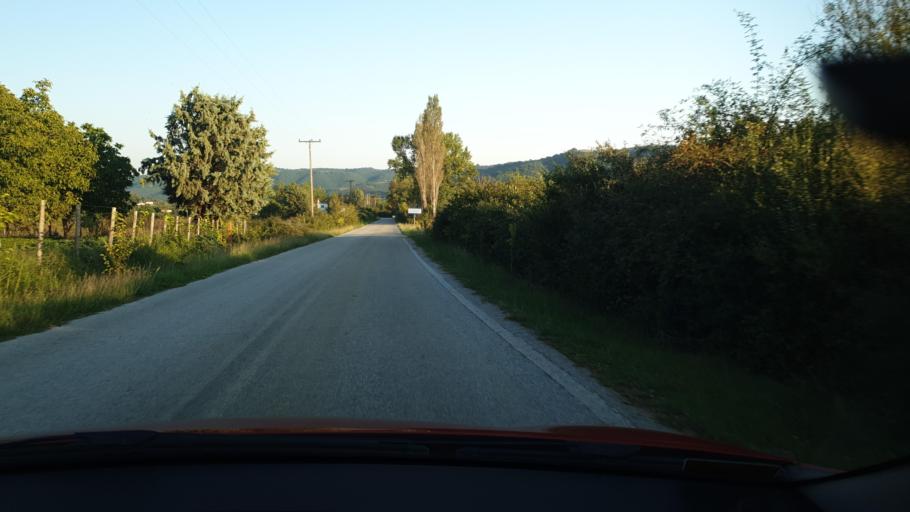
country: GR
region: Central Macedonia
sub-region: Nomos Chalkidikis
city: Galatista
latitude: 40.5221
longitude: 23.2793
